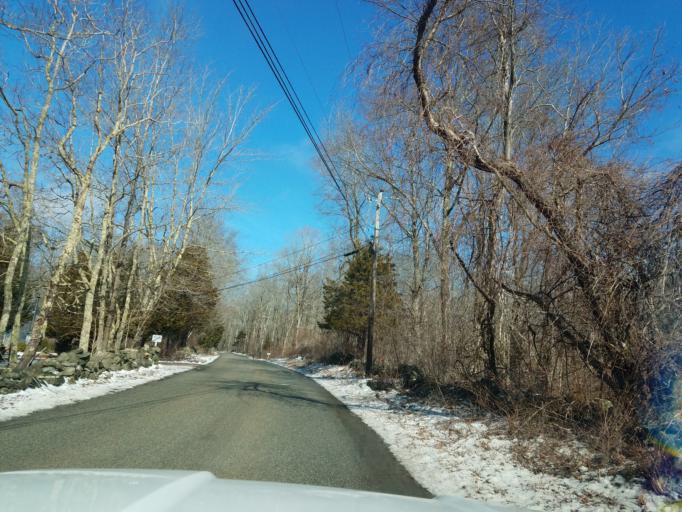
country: US
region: Connecticut
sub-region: New London County
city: Preston City
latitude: 41.4755
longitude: -71.9266
